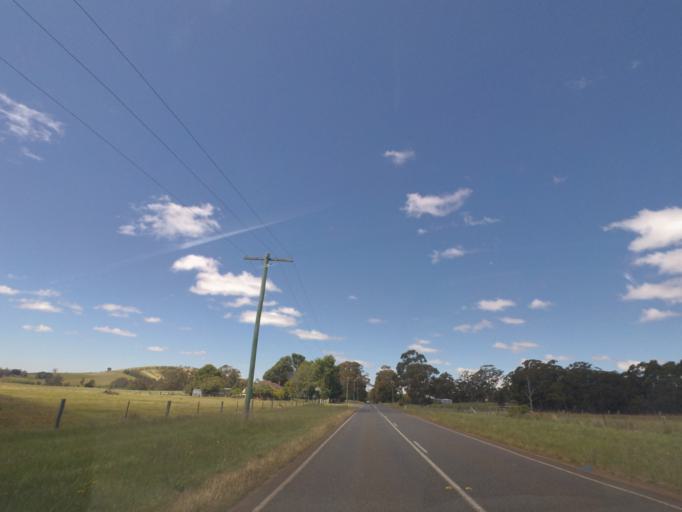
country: AU
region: Victoria
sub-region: Mount Alexander
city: Castlemaine
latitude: -37.3196
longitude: 144.2077
